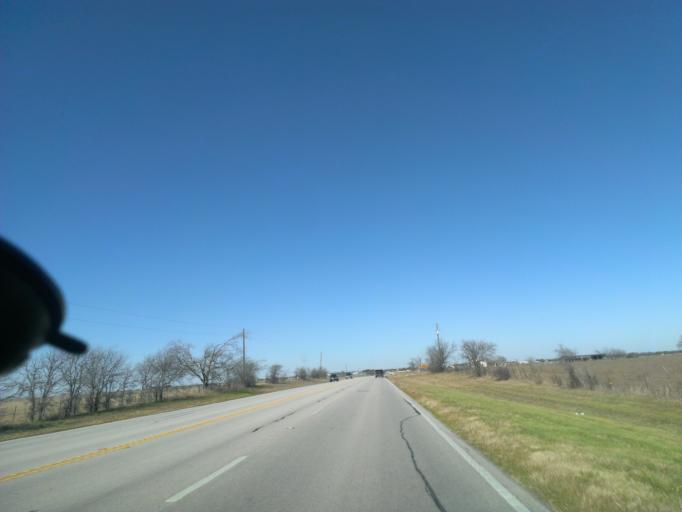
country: US
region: Texas
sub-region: Williamson County
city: Florence
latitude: 30.8668
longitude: -97.9143
